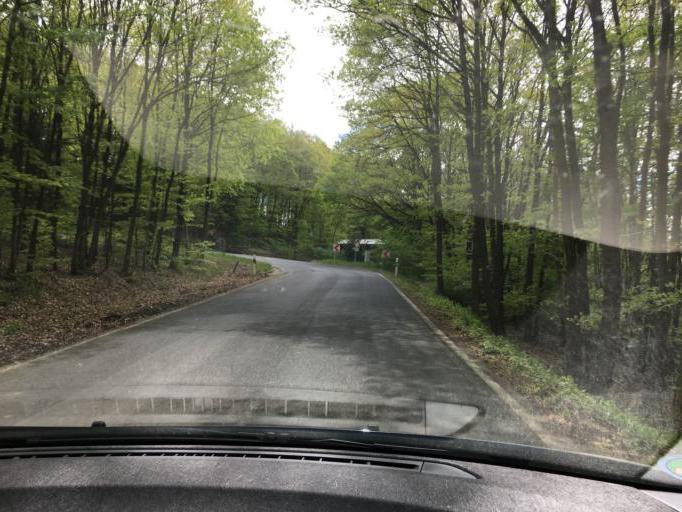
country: DE
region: Rheinland-Pfalz
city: Lind
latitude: 50.4930
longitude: 6.9176
